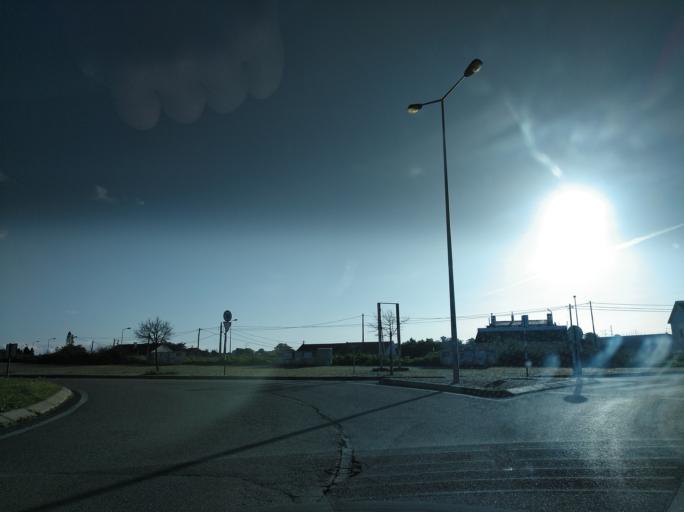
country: PT
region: Setubal
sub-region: Almada
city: Sobreda
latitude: 38.6557
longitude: -9.1886
